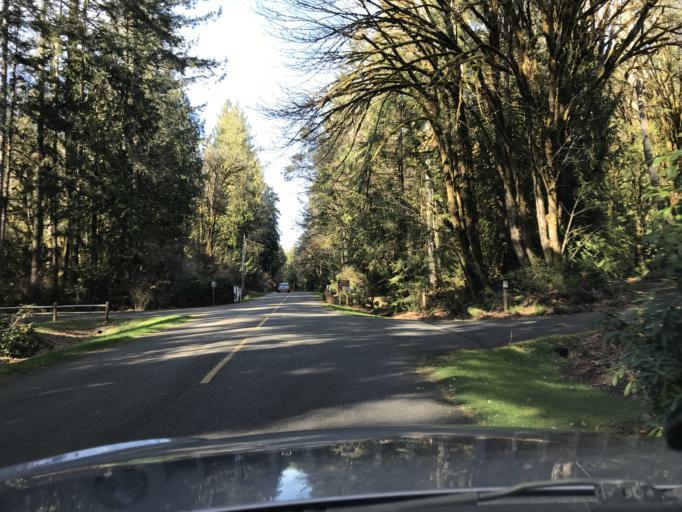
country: US
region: Washington
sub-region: Pierce County
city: Home
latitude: 47.2546
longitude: -122.7484
